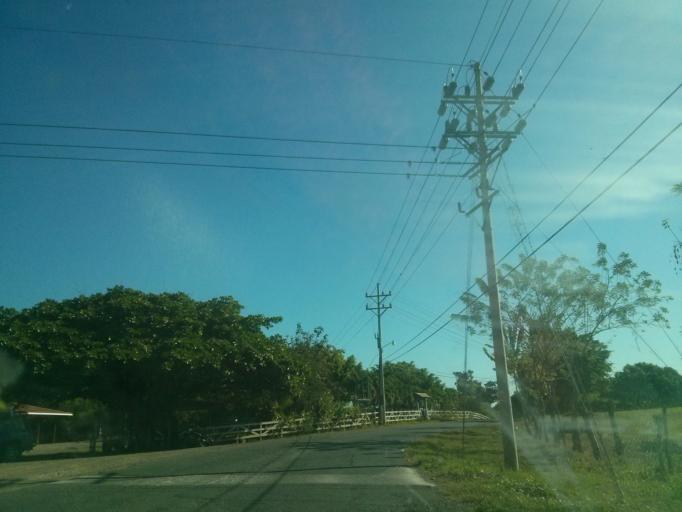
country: CR
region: Puntarenas
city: Paquera
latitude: 9.6935
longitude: -85.0982
